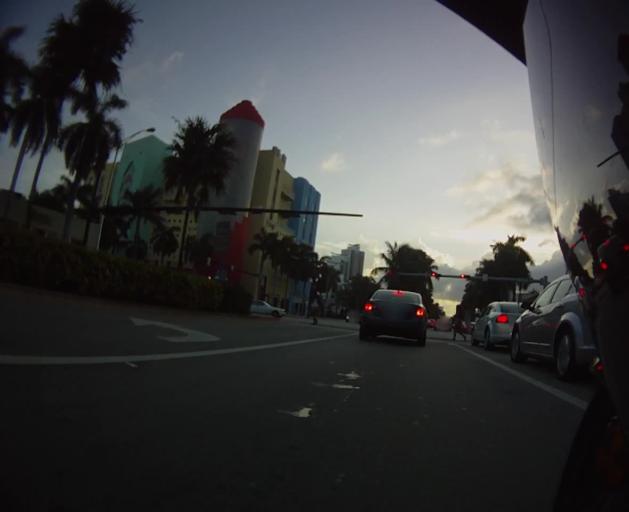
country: US
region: Florida
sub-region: Miami-Dade County
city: Miami Beach
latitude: 25.7746
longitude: -80.1337
